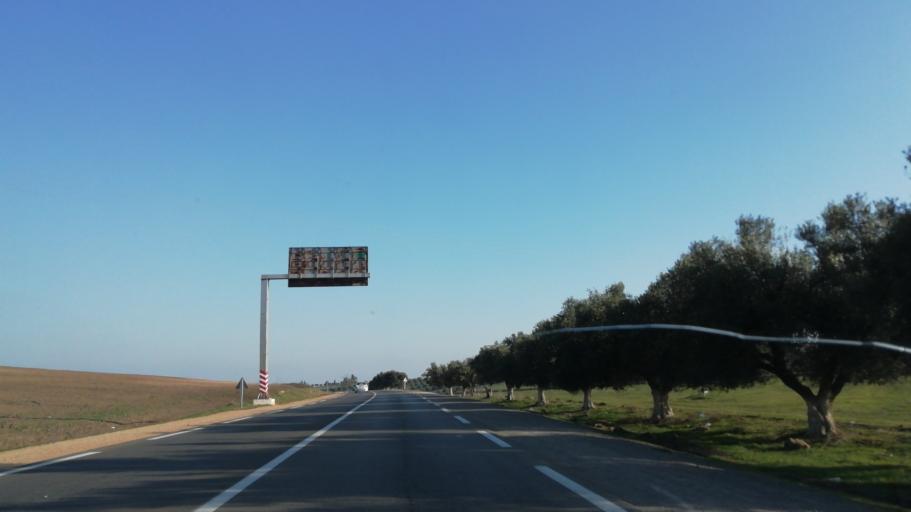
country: DZ
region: Ain Temouchent
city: Hammam Bou Hadjar
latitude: 35.1637
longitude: -0.8734
